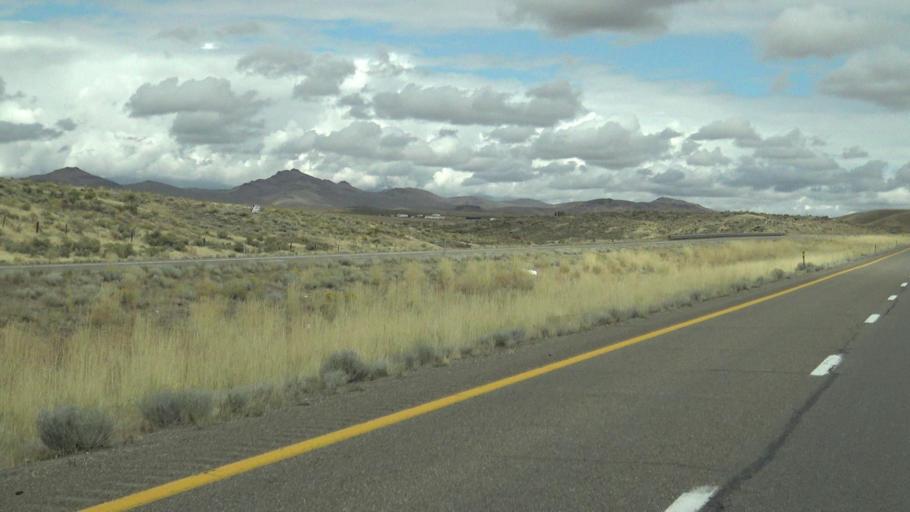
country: US
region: Nevada
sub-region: Elko County
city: Elko
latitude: 40.8868
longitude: -115.7137
